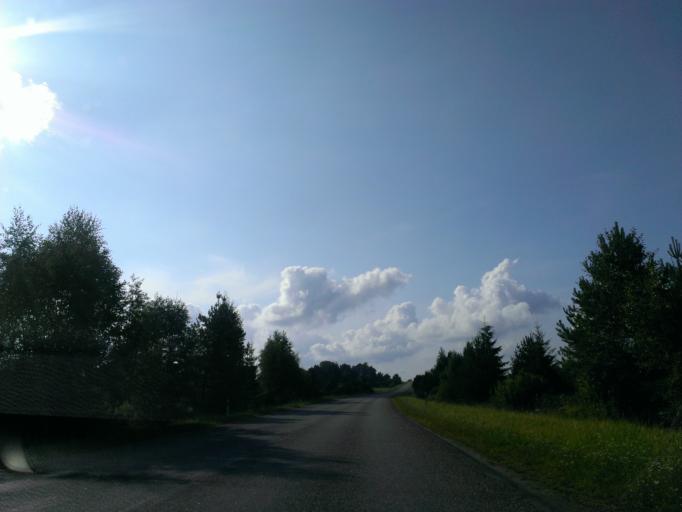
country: LV
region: Priekuli
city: Priekuli
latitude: 57.2953
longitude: 25.4253
